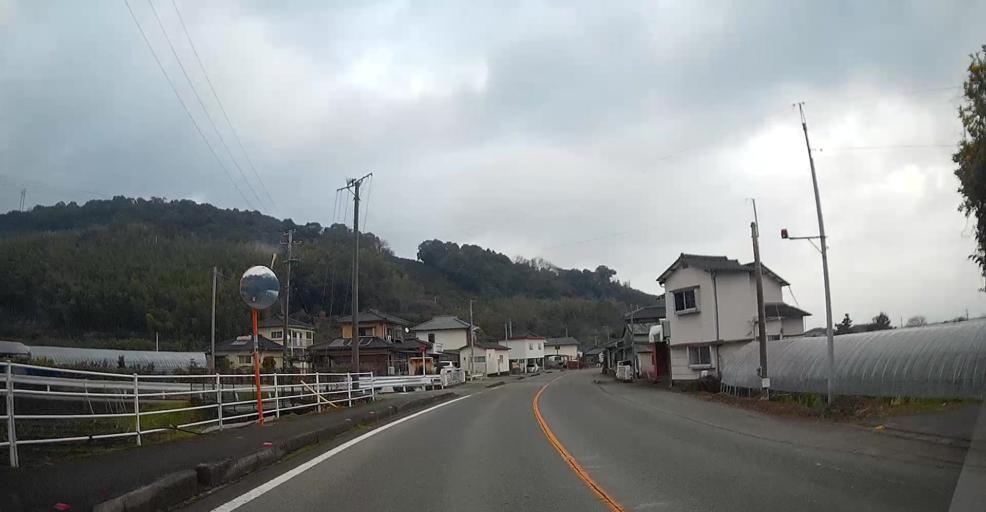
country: JP
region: Kumamoto
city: Matsubase
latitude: 32.6330
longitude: 130.6165
